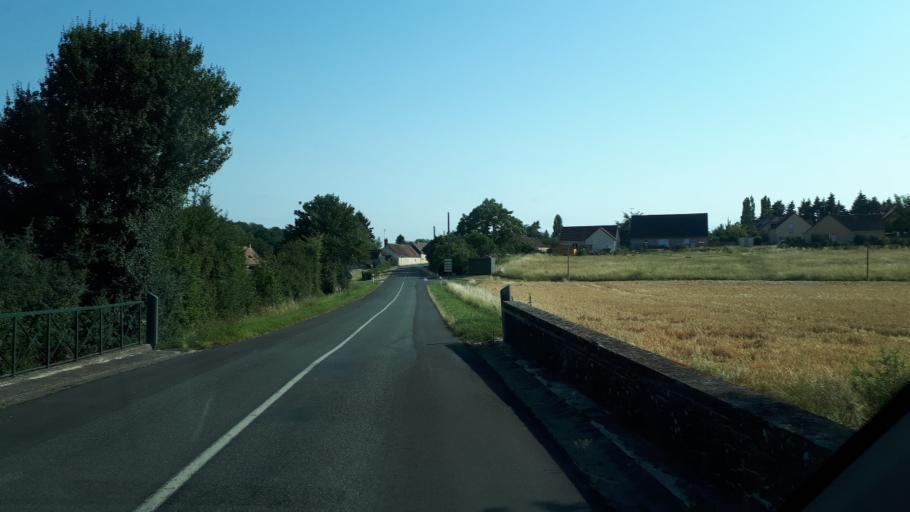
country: FR
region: Centre
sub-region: Departement du Loir-et-Cher
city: Aze
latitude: 47.8556
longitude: 1.0032
